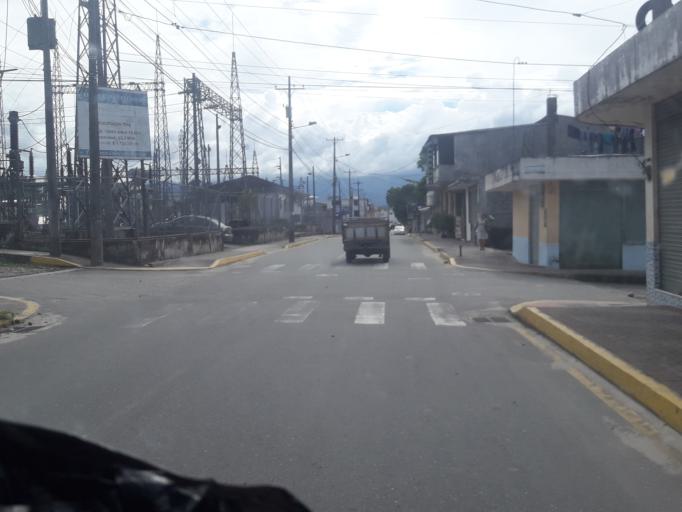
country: EC
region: Napo
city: Tena
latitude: -1.0071
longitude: -77.8106
